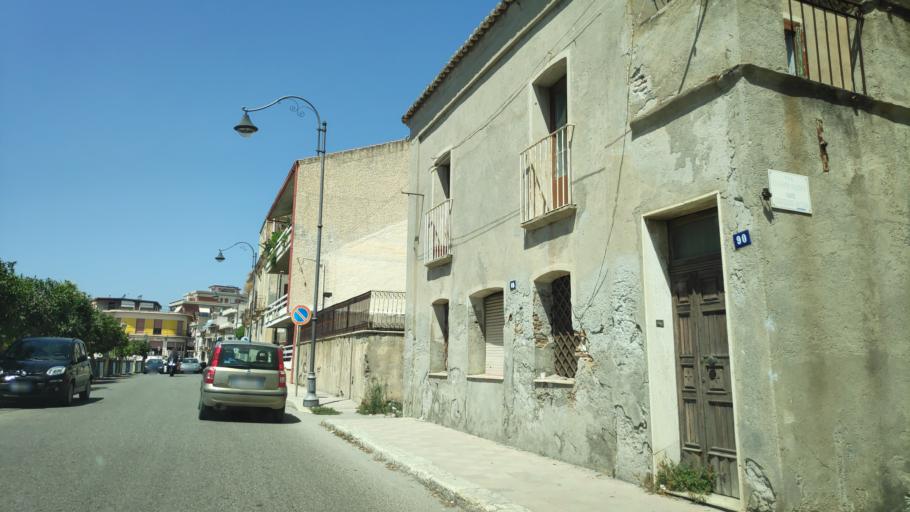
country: IT
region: Calabria
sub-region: Provincia di Reggio Calabria
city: Bova Marina
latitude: 37.9304
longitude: 15.9251
